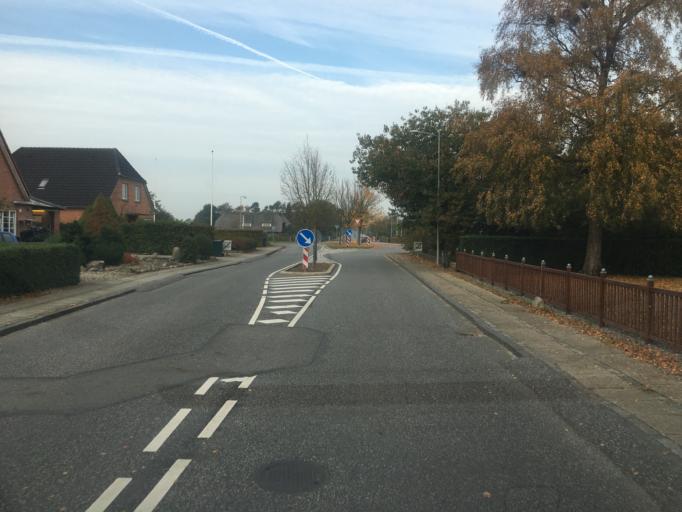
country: DK
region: South Denmark
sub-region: Tonder Kommune
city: Toftlund
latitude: 55.1208
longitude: 9.0677
